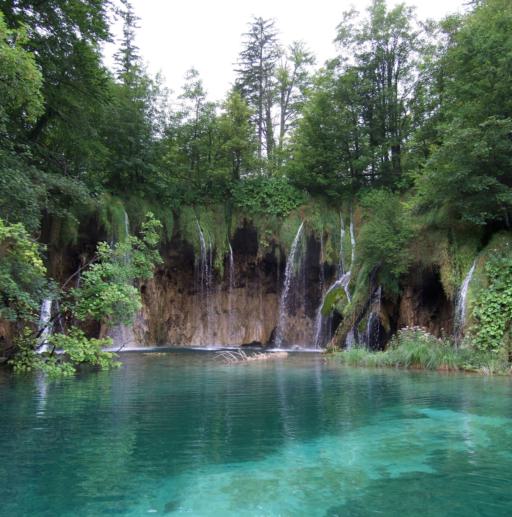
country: HR
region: Licko-Senjska
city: Jezerce
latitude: 44.8759
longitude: 15.6096
